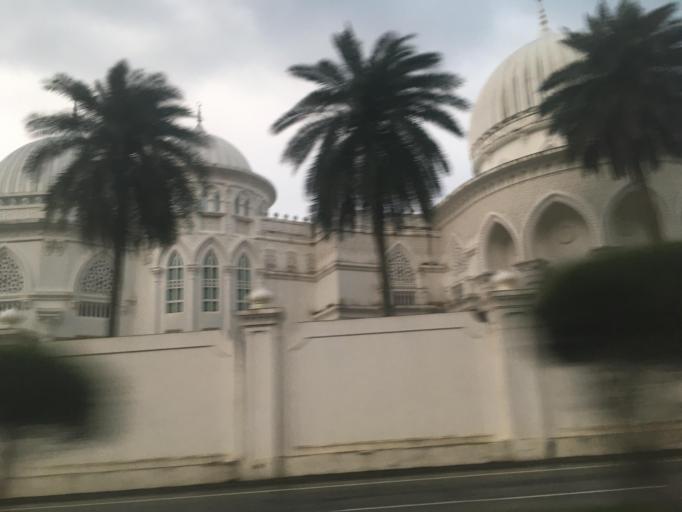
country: TW
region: Taiwan
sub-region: Yilan
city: Yilan
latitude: 24.8869
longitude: 121.8483
